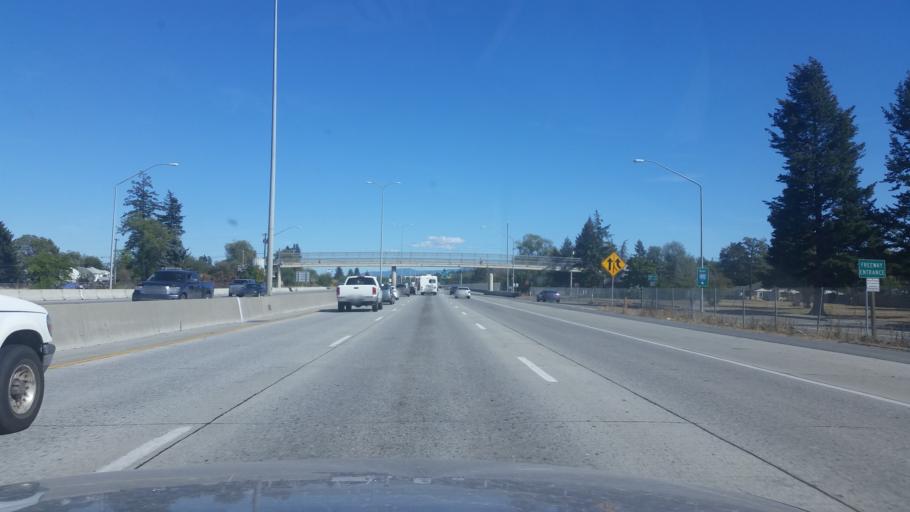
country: US
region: Washington
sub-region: Spokane County
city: Millwood
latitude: 47.6538
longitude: -117.3442
